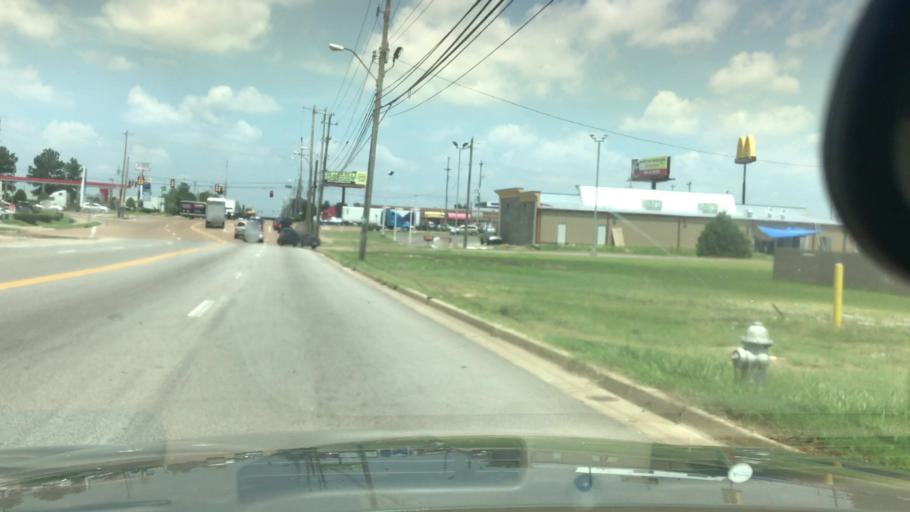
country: US
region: Mississippi
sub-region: De Soto County
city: Southaven
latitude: 35.0191
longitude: -89.9367
